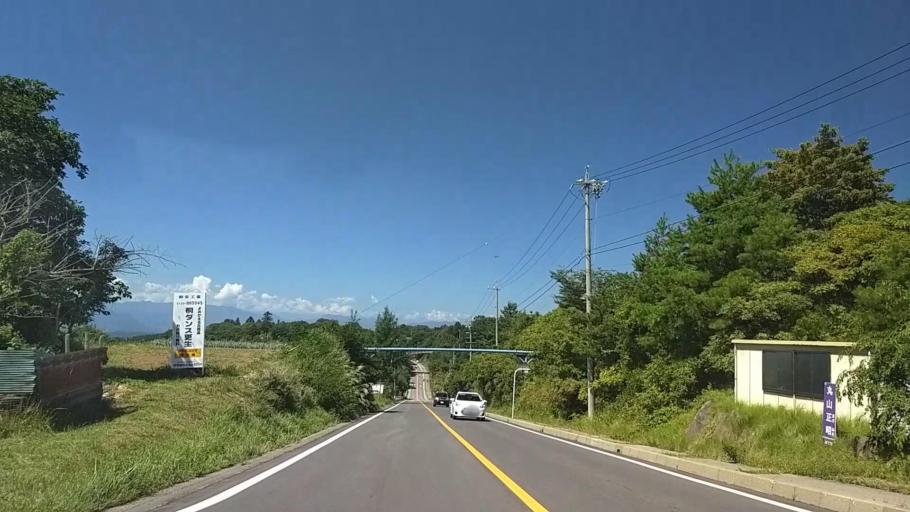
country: JP
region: Nagano
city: Komoro
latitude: 36.3509
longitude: 138.4168
